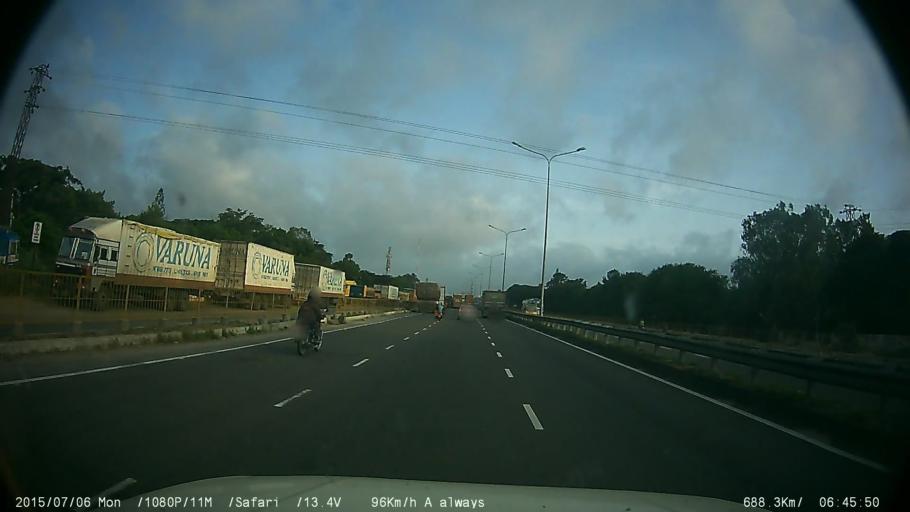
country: IN
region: Tamil Nadu
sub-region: Krishnagiri
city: Hosur
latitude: 12.7593
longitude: 77.7976
